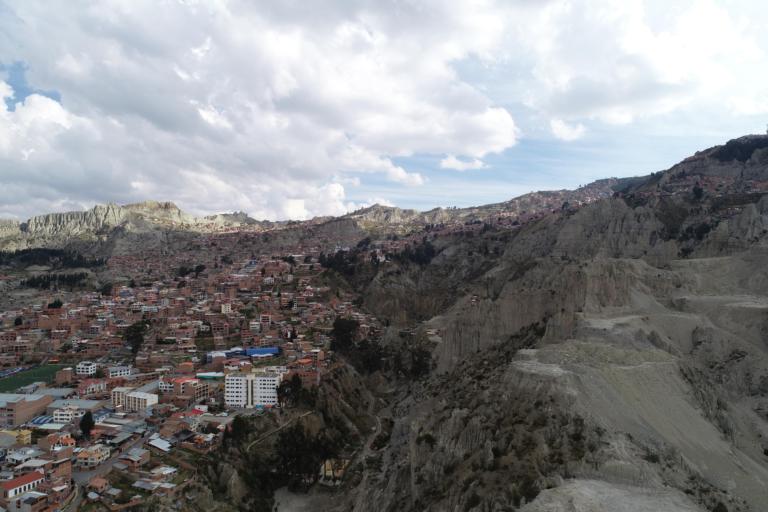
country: BO
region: La Paz
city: La Paz
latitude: -16.5232
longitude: -68.1268
